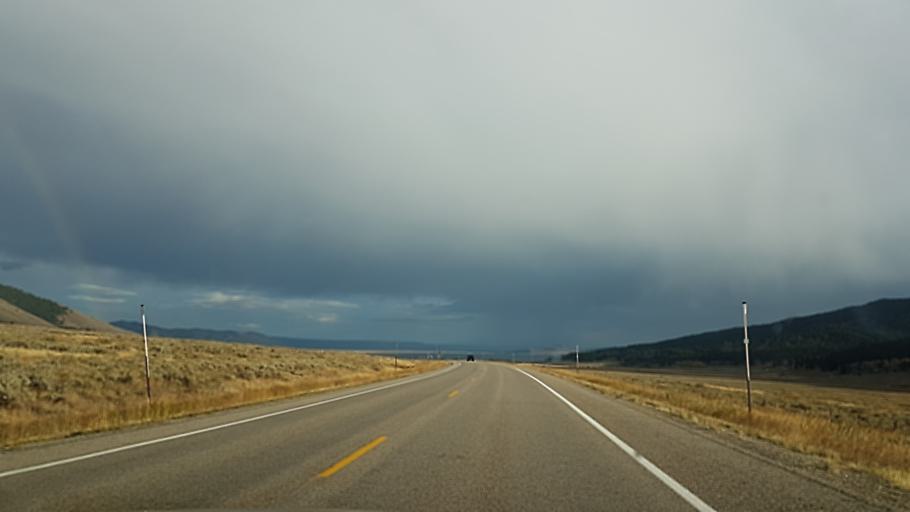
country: US
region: Montana
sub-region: Gallatin County
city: West Yellowstone
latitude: 44.6997
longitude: -111.4590
